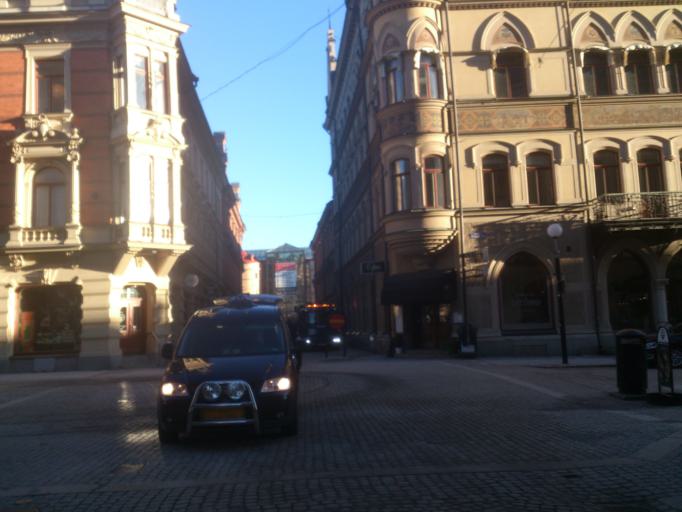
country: SE
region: Vaesternorrland
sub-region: Sundsvalls Kommun
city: Sundsvall
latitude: 62.3905
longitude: 17.3115
